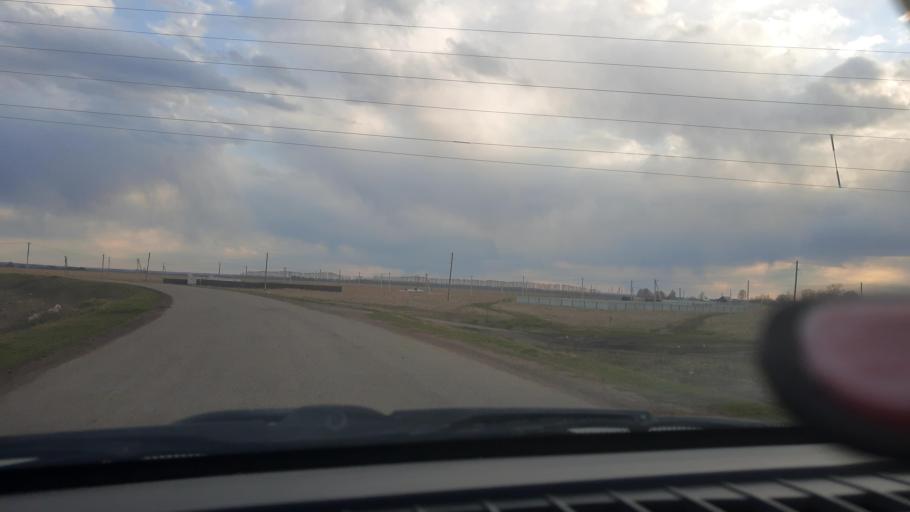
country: RU
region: Bashkortostan
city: Asanovo
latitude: 54.9594
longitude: 55.5362
